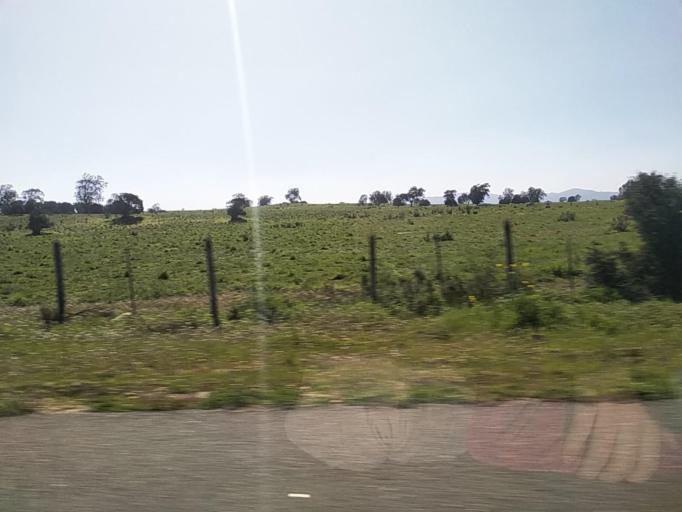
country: CL
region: Valparaiso
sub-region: San Antonio Province
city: El Tabo
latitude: -33.4067
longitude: -71.5392
